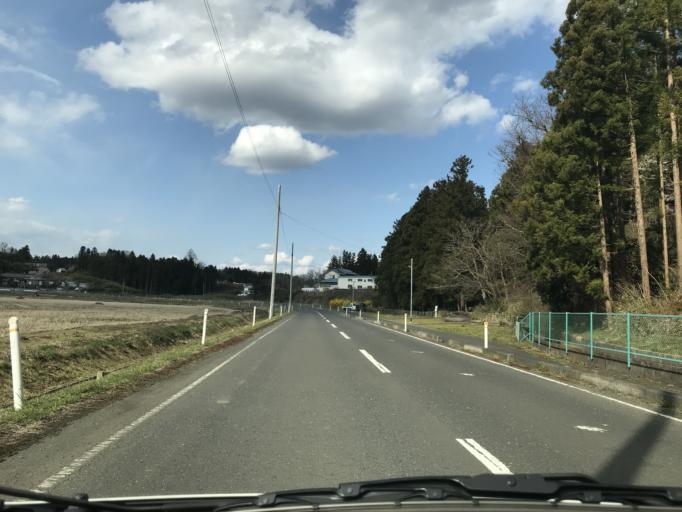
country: JP
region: Iwate
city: Ichinoseki
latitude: 38.7478
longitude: 141.1868
